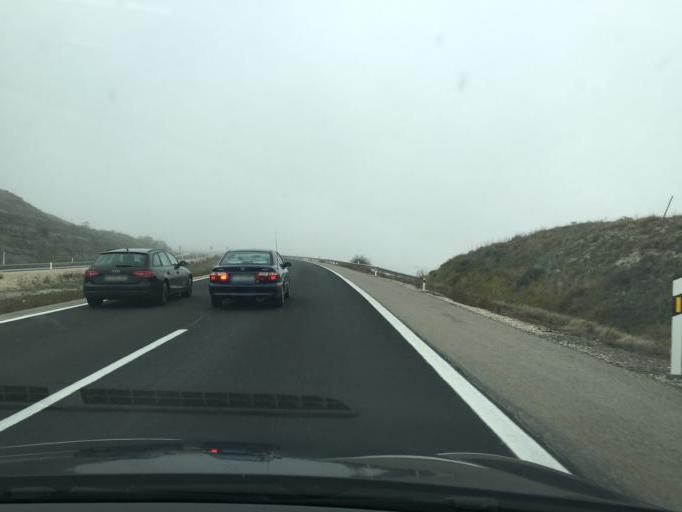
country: ES
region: Castille and Leon
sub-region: Provincia de Burgos
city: Pancorbo
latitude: 42.6235
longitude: -3.1350
